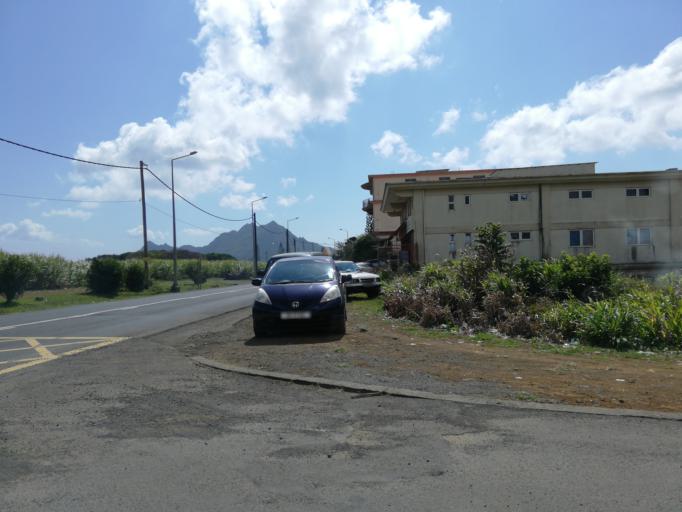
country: MU
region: Moka
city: Verdun
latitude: -20.2269
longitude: 57.5428
